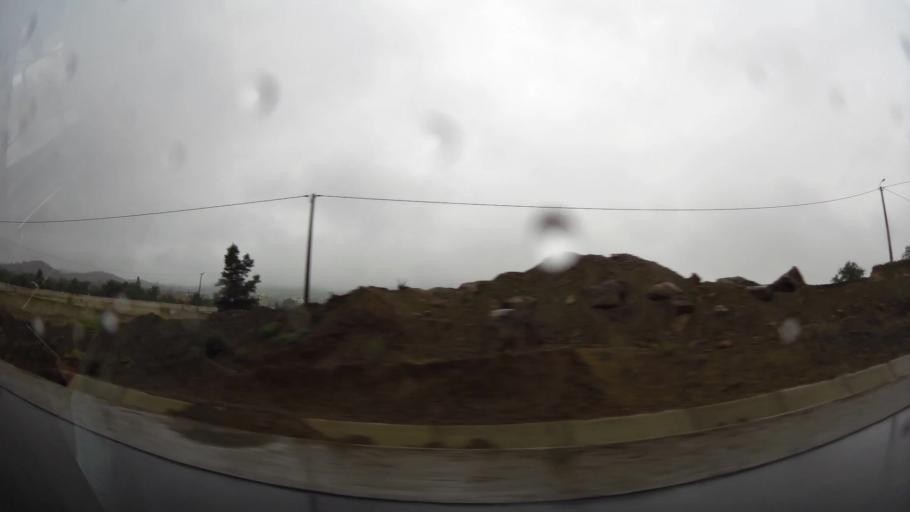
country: MA
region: Oriental
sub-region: Nador
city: Midar
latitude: 34.8565
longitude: -3.7222
